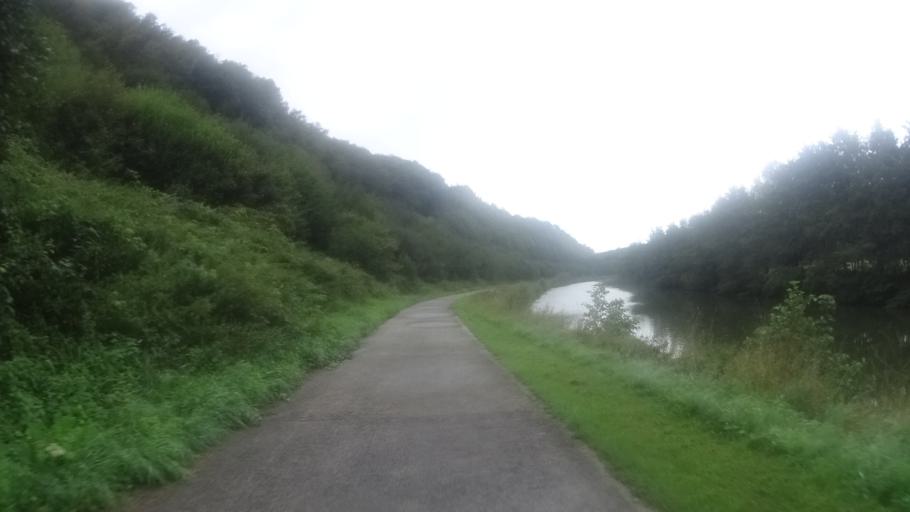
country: BE
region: Wallonia
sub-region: Province du Hainaut
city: Thuin
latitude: 50.3508
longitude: 4.3083
